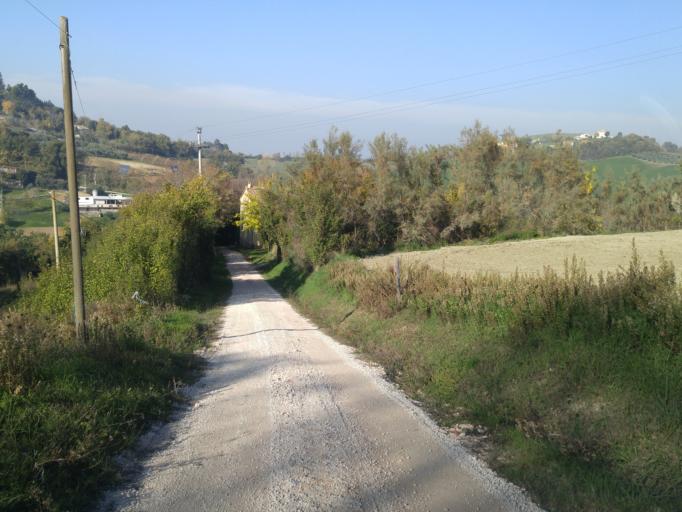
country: IT
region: The Marches
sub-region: Provincia di Pesaro e Urbino
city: Montemaggiore al Metauro
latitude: 43.7327
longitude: 12.9527
